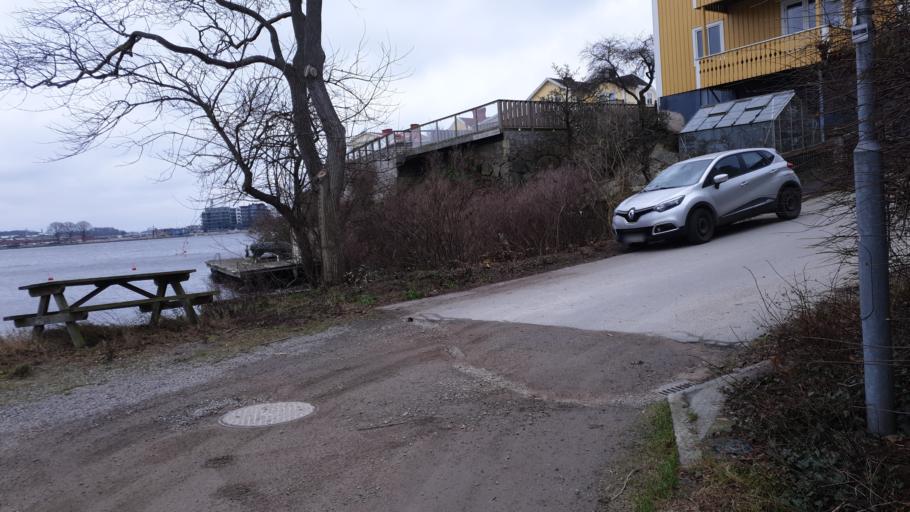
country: SE
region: Blekinge
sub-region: Karlskrona Kommun
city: Karlskrona
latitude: 56.1650
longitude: 15.5711
